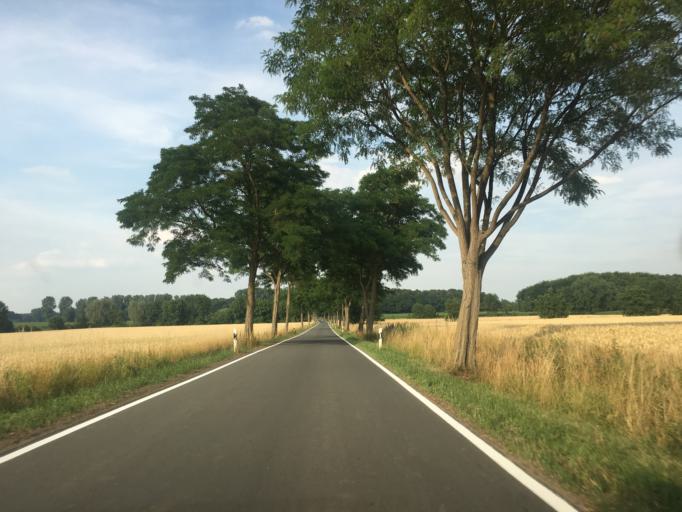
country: DE
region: North Rhine-Westphalia
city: Ludinghausen
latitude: 51.7971
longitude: 7.3785
